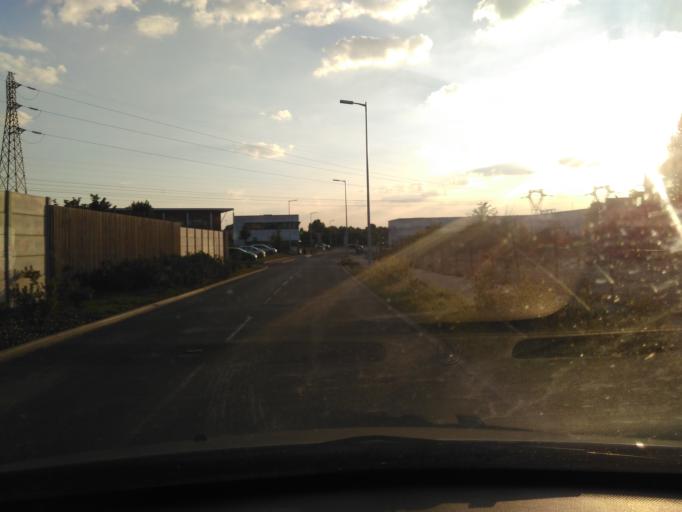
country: FR
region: Poitou-Charentes
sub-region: Departement de la Charente-Maritime
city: Puilboreau
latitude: 46.1763
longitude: -1.1180
